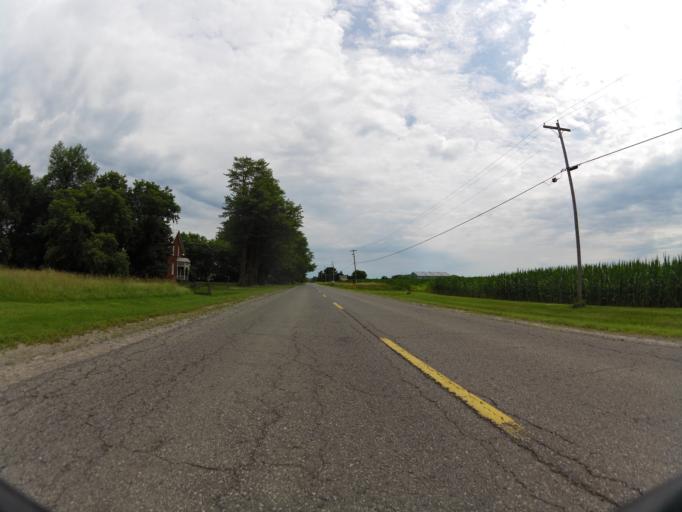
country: CA
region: Ontario
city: Bells Corners
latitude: 45.0168
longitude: -75.7207
